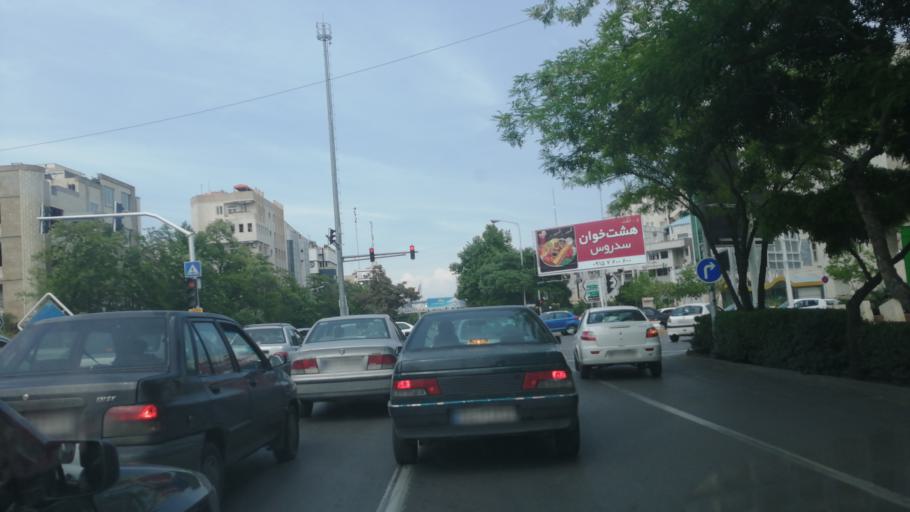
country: IR
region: Razavi Khorasan
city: Mashhad
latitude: 36.3192
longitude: 59.5650
